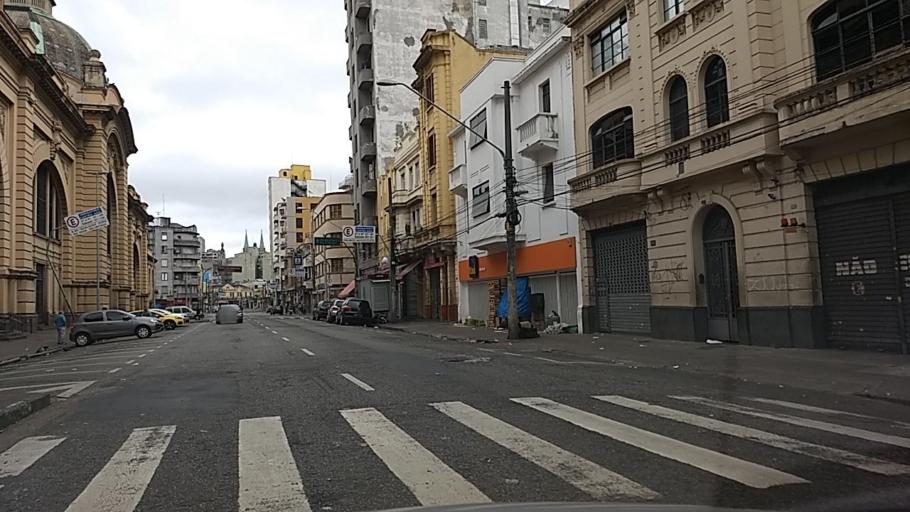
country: BR
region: Sao Paulo
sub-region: Sao Paulo
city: Sao Paulo
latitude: -23.5411
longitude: -46.6298
